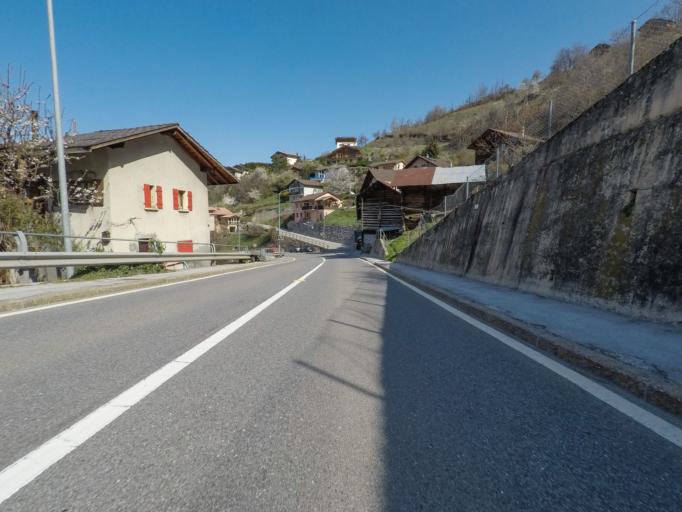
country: CH
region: Valais
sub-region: Conthey District
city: Basse-Nendaz
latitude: 46.1901
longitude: 7.3268
